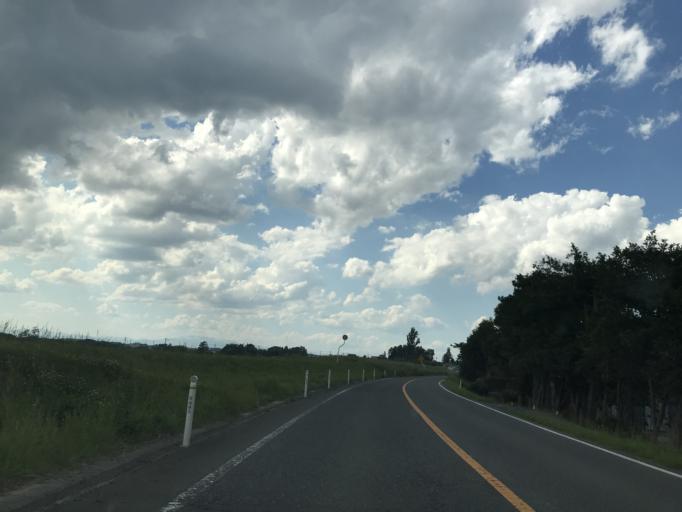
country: JP
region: Miyagi
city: Wakuya
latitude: 38.6666
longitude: 141.2133
